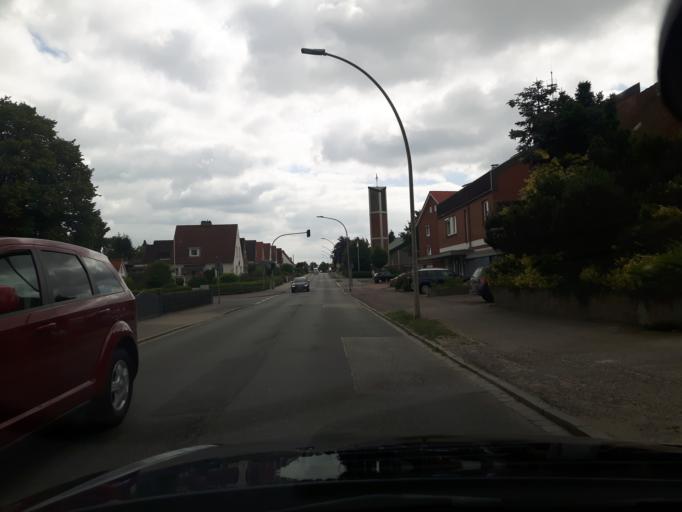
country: DE
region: Schleswig-Holstein
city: Neustadt in Holstein
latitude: 54.1052
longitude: 10.8248
